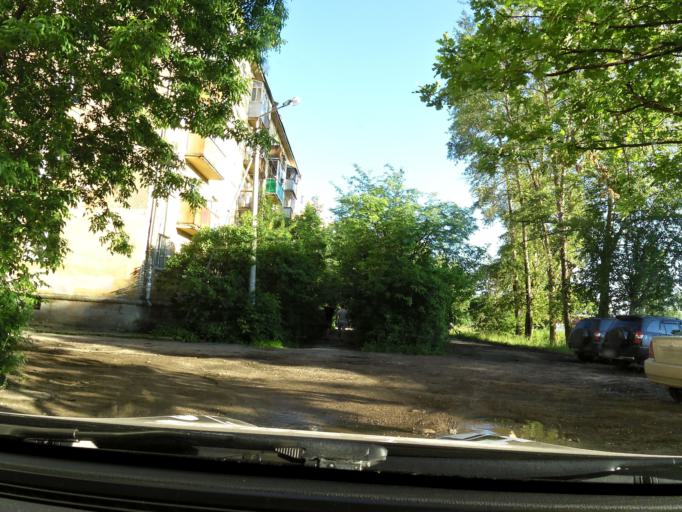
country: RU
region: Vologda
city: Vologda
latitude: 59.2195
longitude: 39.9129
